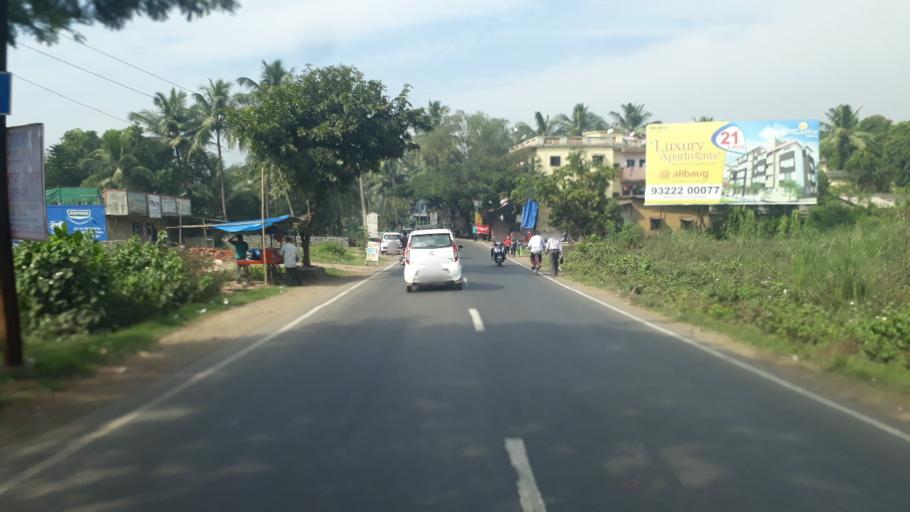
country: IN
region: Maharashtra
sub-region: Raigarh
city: Alibag
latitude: 18.6883
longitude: 72.9849
